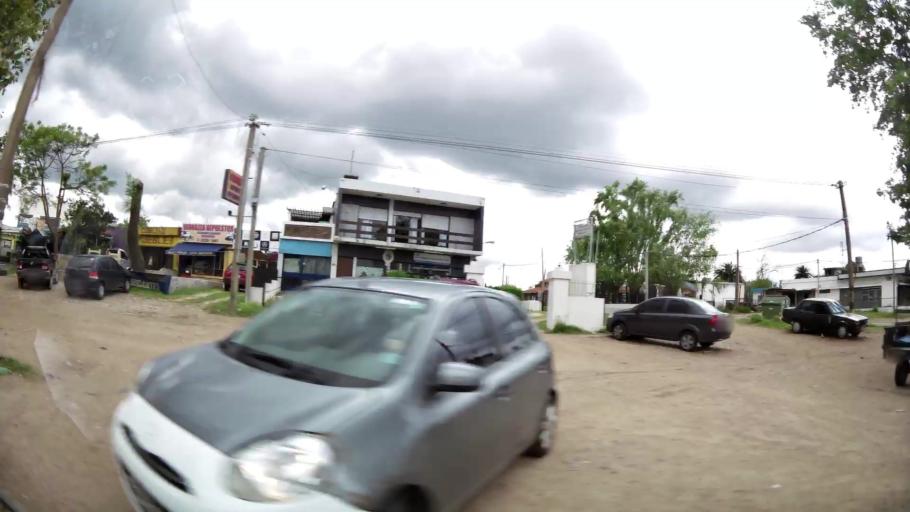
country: UY
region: Canelones
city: Toledo
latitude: -34.8191
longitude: -56.1395
